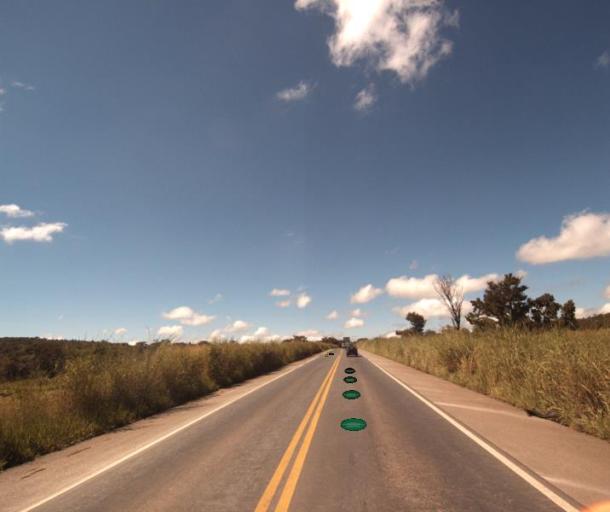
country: BR
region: Goias
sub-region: Jaragua
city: Jaragua
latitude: -15.6500
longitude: -49.3656
